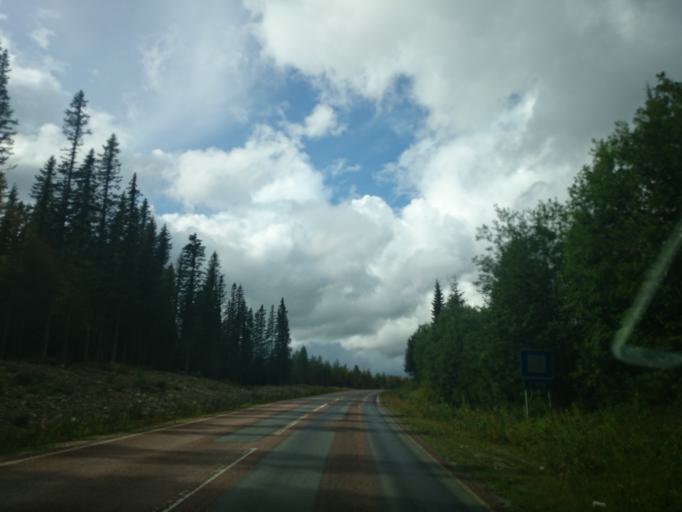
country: SE
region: Jaemtland
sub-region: Bergs Kommun
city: Hoverberg
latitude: 62.4724
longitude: 14.2084
